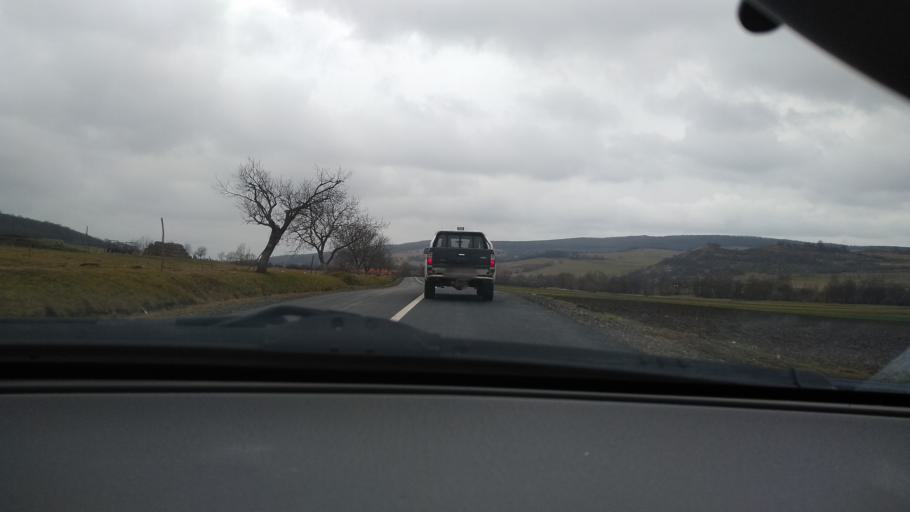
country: RO
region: Mures
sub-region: Comuna Bereni
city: Bereni
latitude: 46.5585
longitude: 24.8803
